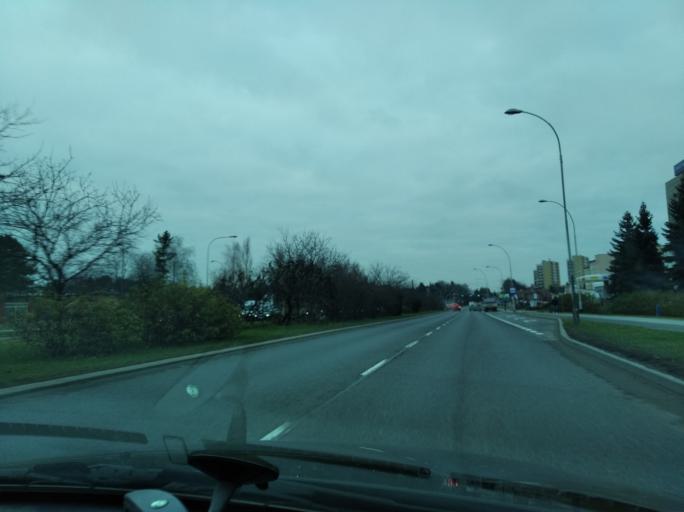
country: PL
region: Subcarpathian Voivodeship
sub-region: Rzeszow
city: Rzeszow
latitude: 50.0280
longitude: 21.9766
